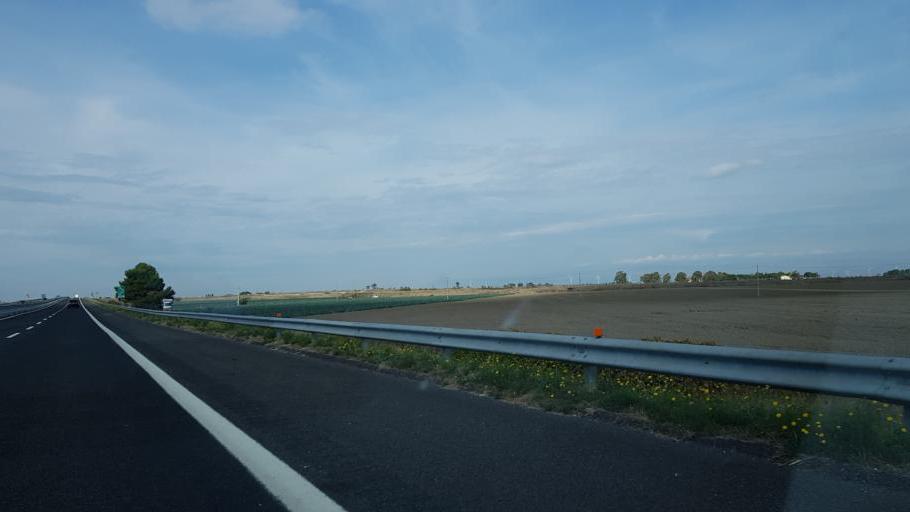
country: IT
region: Apulia
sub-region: Provincia di Foggia
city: Carapelle
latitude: 41.3753
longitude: 15.7626
